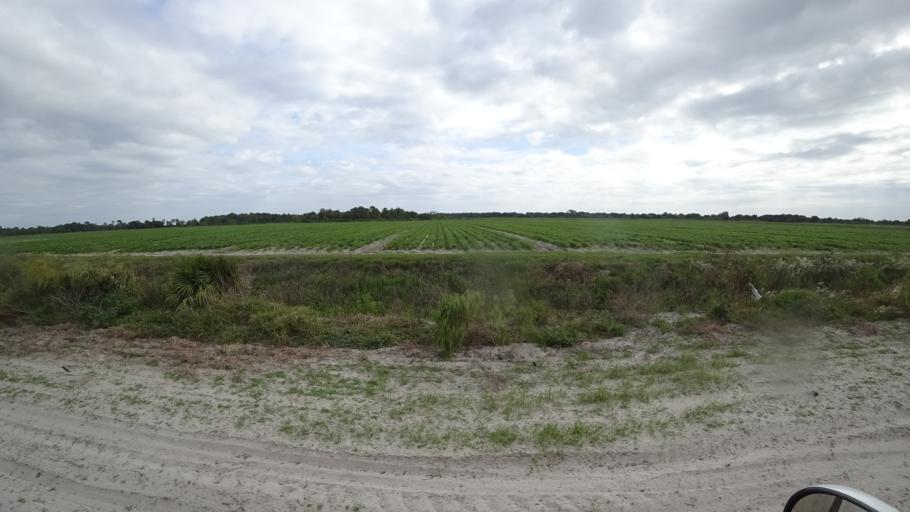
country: US
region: Florida
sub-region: Hillsborough County
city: Wimauma
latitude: 27.5606
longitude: -82.2945
